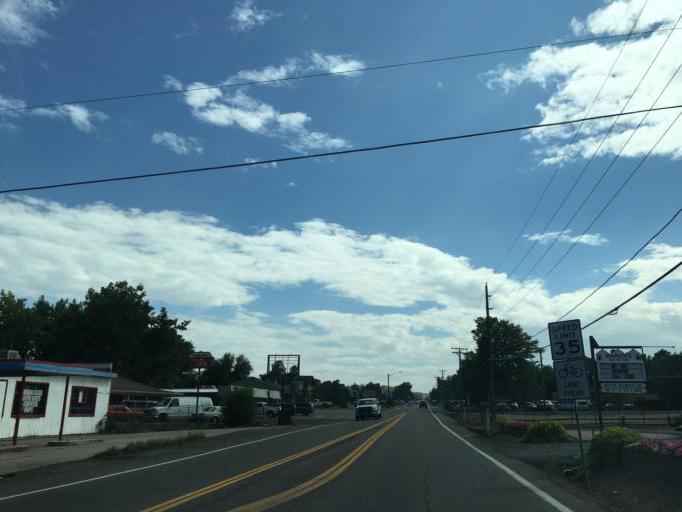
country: US
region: Colorado
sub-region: Jefferson County
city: Applewood
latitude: 39.7555
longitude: -105.1424
